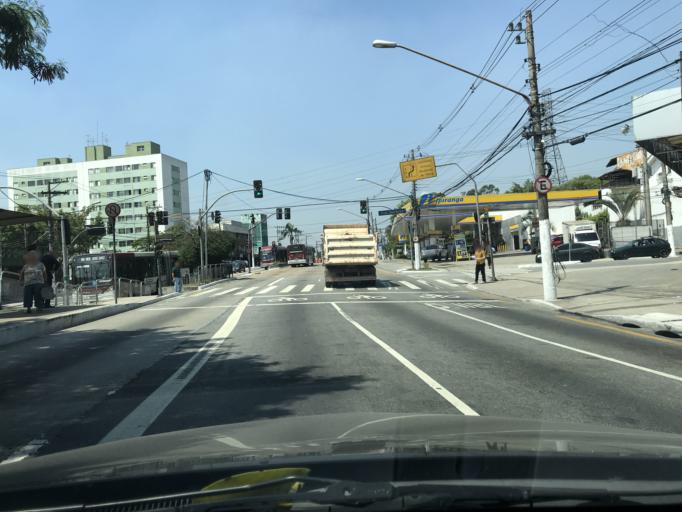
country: BR
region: Sao Paulo
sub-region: Taboao Da Serra
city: Taboao da Serra
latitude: -23.6678
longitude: -46.7302
